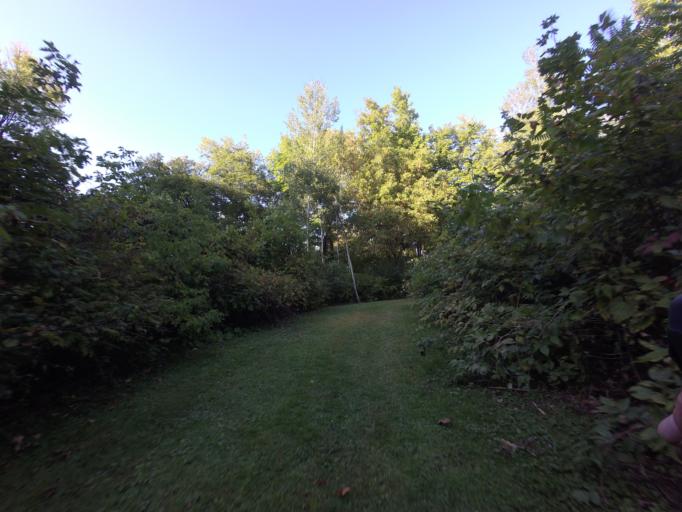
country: CA
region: Ontario
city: Ottawa
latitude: 45.3884
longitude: -75.6734
